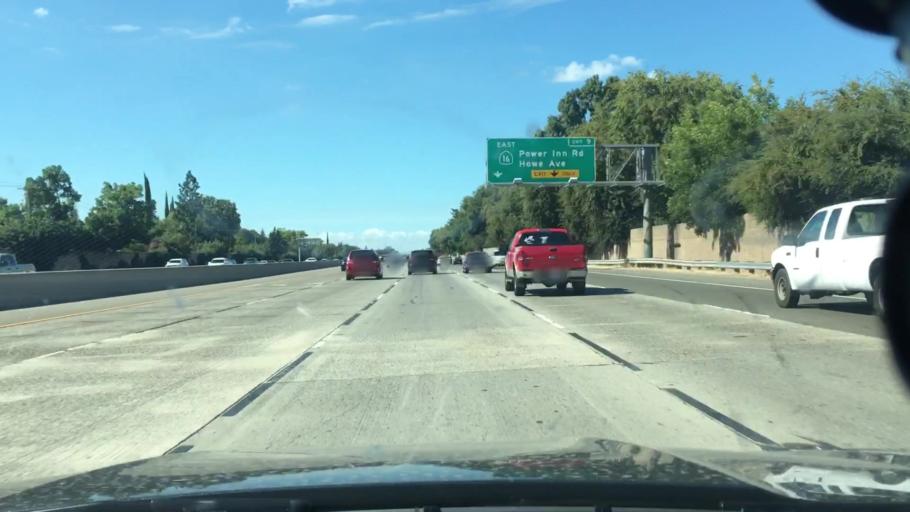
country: US
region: California
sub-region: Sacramento County
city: Rosemont
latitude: 38.5569
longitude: -121.3956
